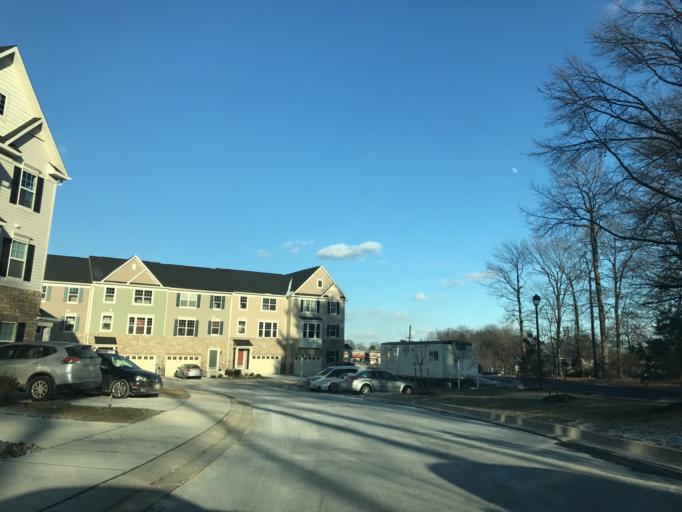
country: US
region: Maryland
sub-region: Baltimore County
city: Middle River
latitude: 39.3237
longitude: -76.4428
